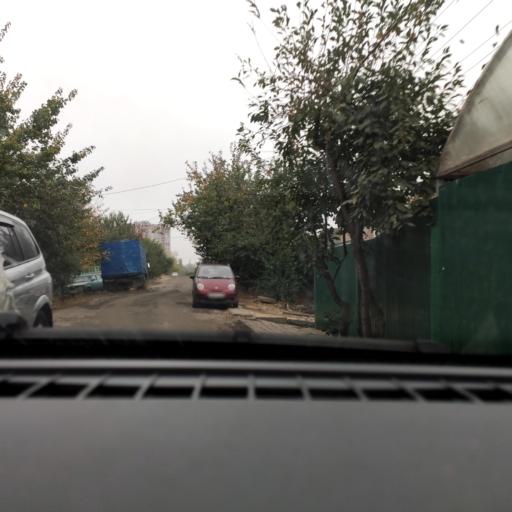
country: RU
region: Voronezj
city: Voronezh
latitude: 51.6663
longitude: 39.2844
